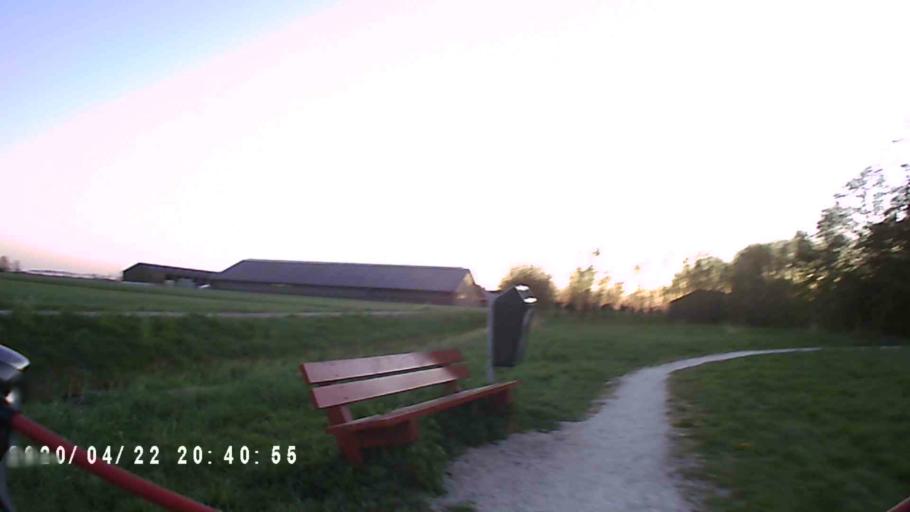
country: NL
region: Groningen
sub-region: Gemeente Winsum
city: Winsum
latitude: 53.3231
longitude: 6.5355
